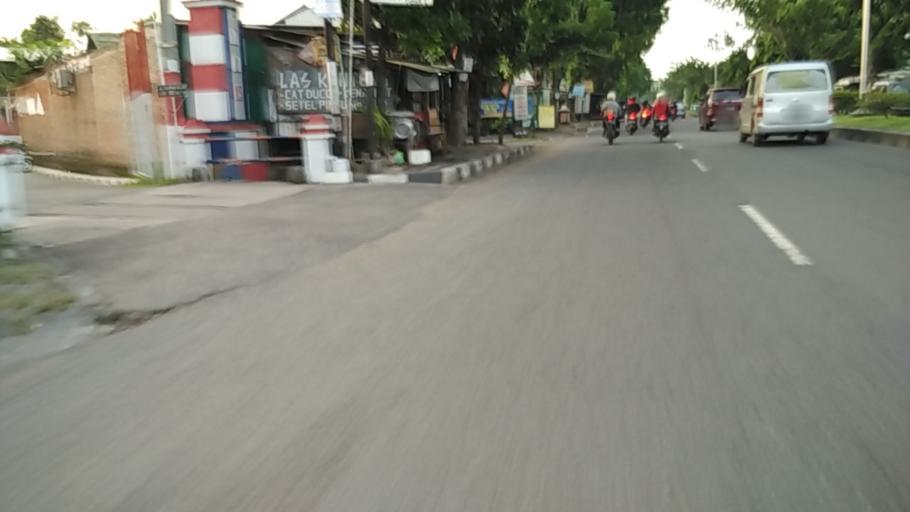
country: ID
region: Central Java
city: Semarang
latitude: -6.9844
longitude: 110.4541
